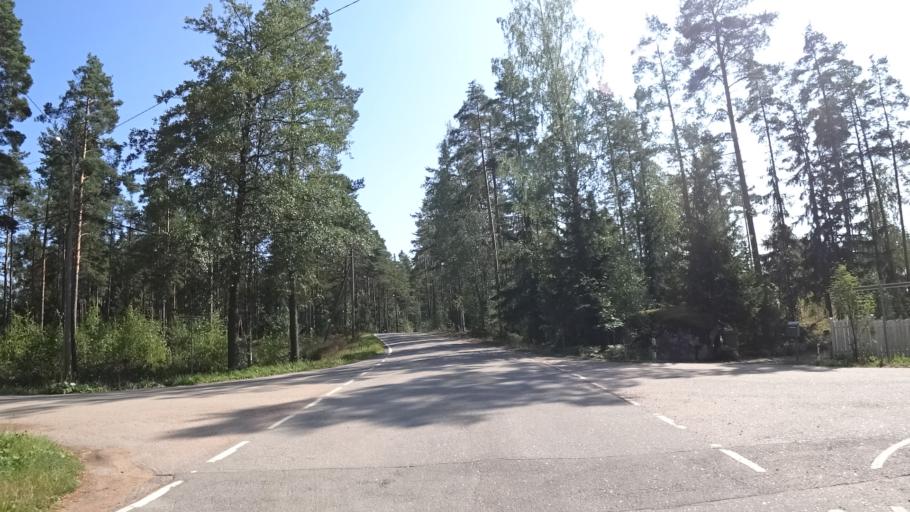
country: FI
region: Kymenlaakso
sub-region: Kotka-Hamina
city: Karhula
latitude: 60.5579
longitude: 26.9003
